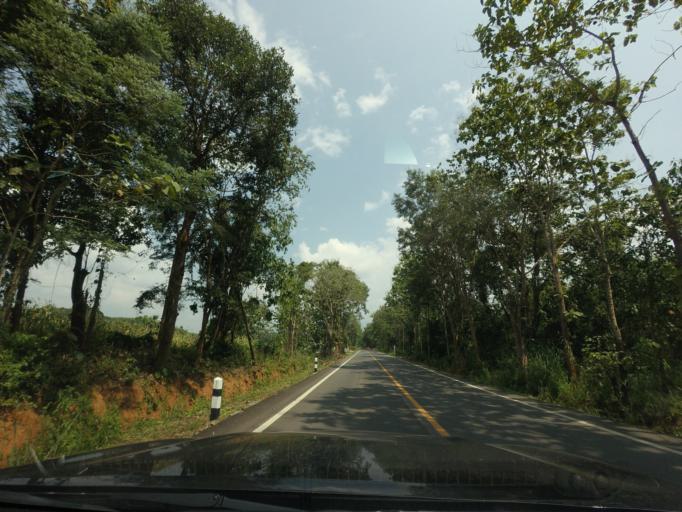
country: TH
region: Nan
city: Santi Suk
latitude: 18.9761
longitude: 100.9293
